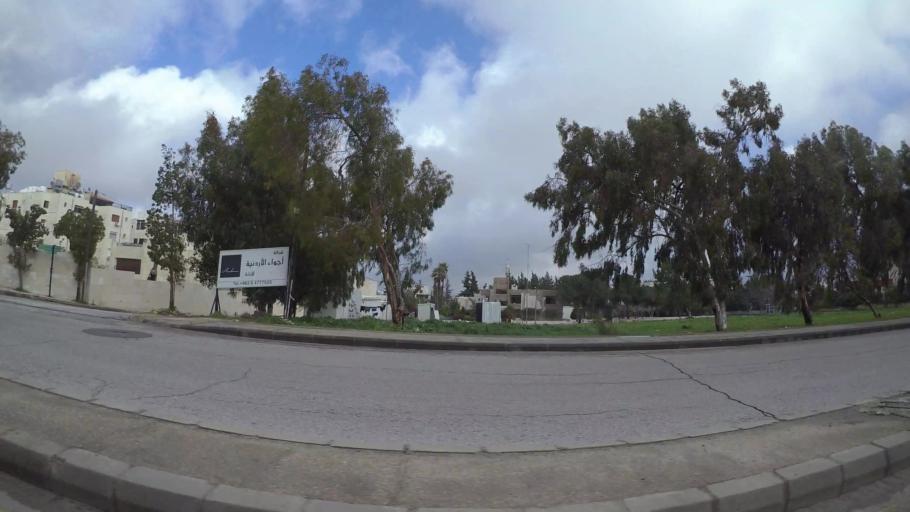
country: JO
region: Amman
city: Wadi as Sir
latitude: 31.9555
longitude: 35.8778
